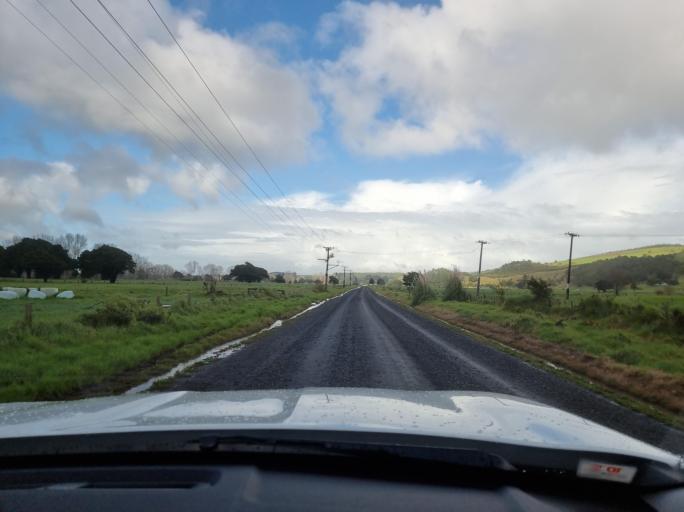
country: NZ
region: Northland
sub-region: Kaipara District
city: Dargaville
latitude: -35.7941
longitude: 173.7312
